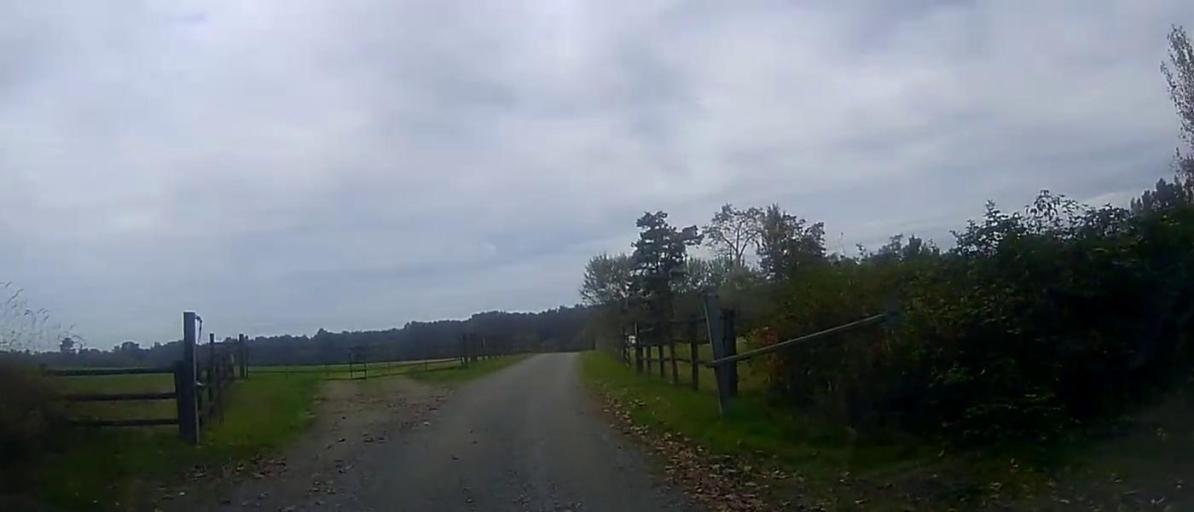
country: US
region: Washington
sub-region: Skagit County
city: Clear Lake
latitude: 48.4686
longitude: -122.2579
